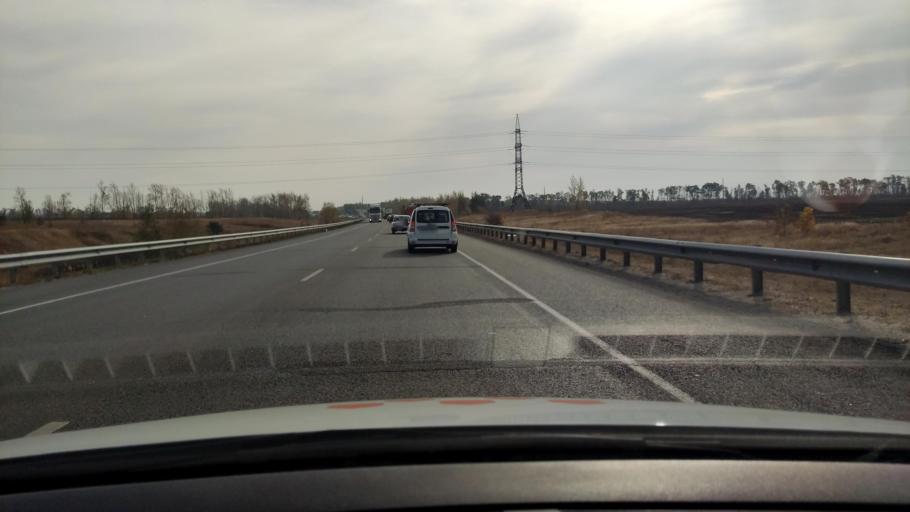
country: RU
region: Voronezj
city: Novaya Usman'
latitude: 51.6978
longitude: 39.4328
